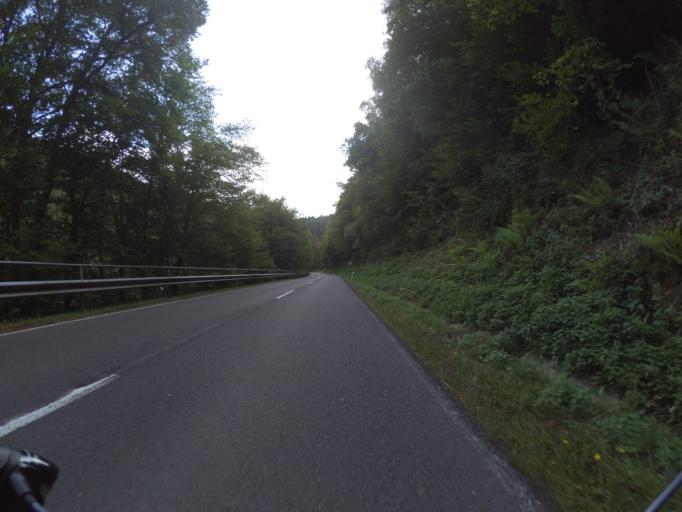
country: DE
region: Rheinland-Pfalz
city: Budlich
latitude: 49.7940
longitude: 6.8990
